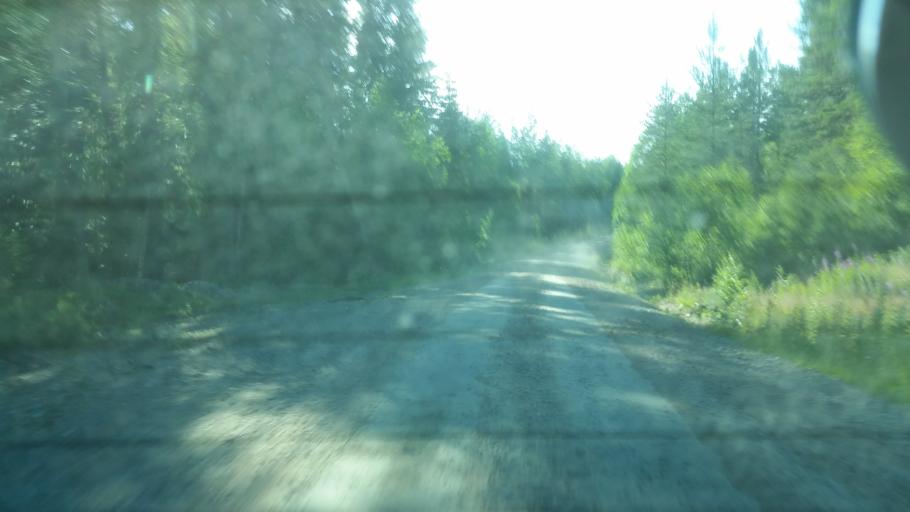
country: SE
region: Vaesternorrland
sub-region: Ange Kommun
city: Ange
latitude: 62.1942
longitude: 15.5961
